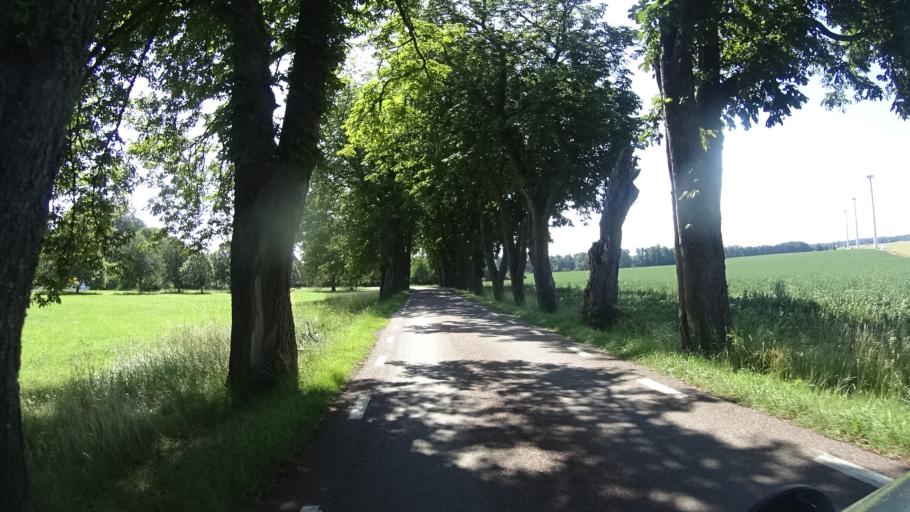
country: SE
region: OEstergoetland
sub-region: Vadstena Kommun
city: Herrestad
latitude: 58.3226
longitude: 14.8368
